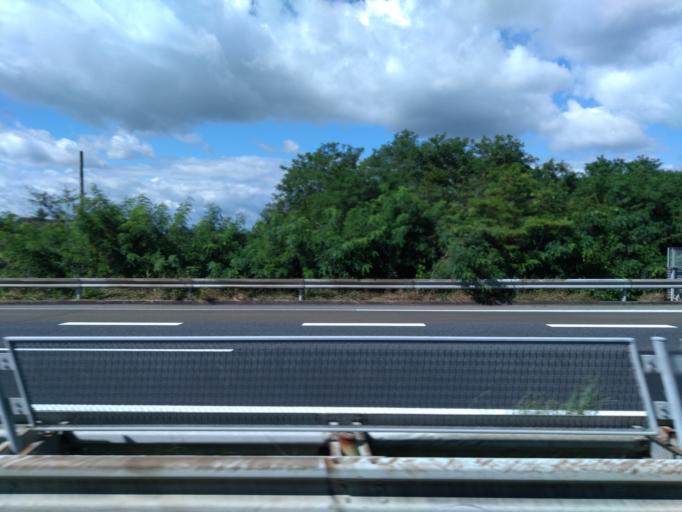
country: JP
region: Iwate
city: Ichinoseki
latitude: 38.8380
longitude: 141.0992
